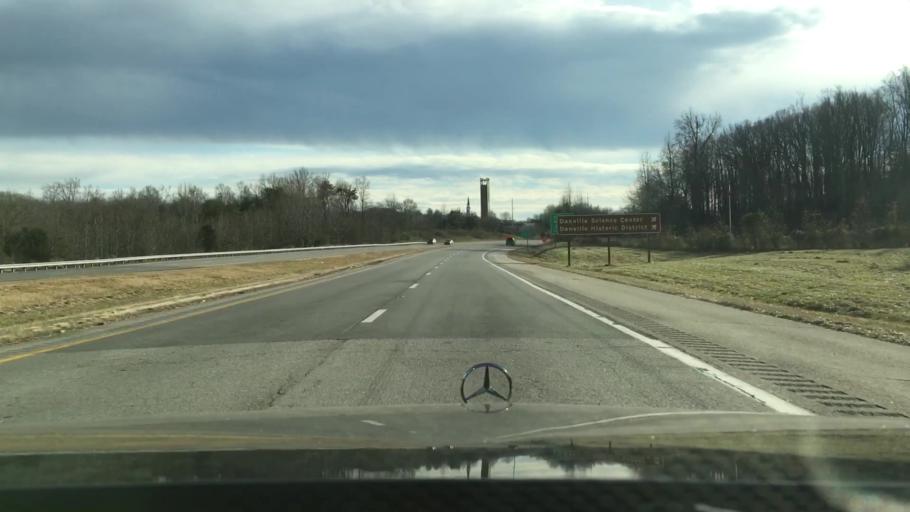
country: US
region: Virginia
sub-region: City of Danville
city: Danville
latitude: 36.5930
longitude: -79.3568
